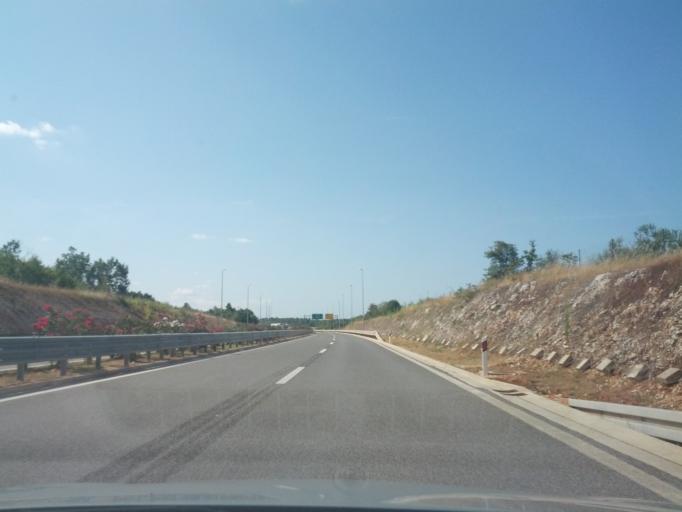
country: HR
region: Istarska
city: Karojba
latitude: 45.2231
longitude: 13.7219
